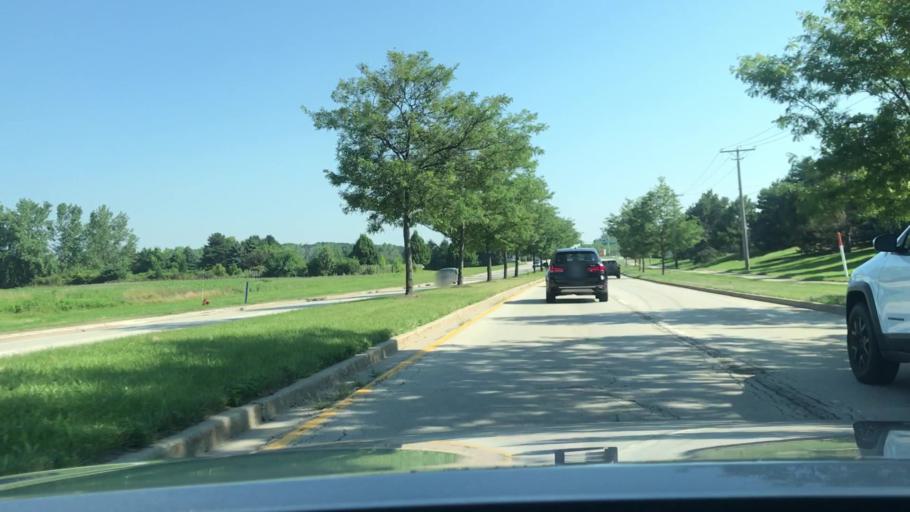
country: US
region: Illinois
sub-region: DuPage County
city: Warrenville
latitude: 41.8052
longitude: -88.2390
